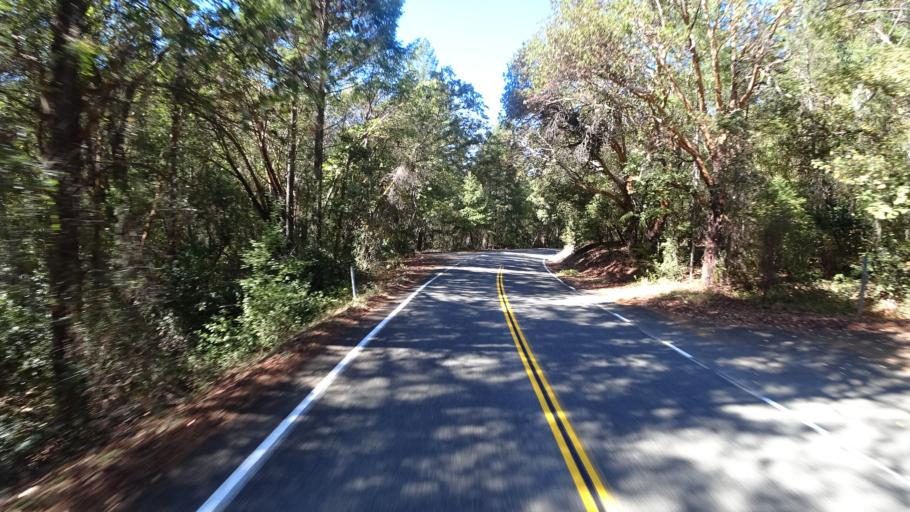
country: US
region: California
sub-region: Siskiyou County
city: Happy Camp
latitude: 41.3754
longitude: -123.4525
